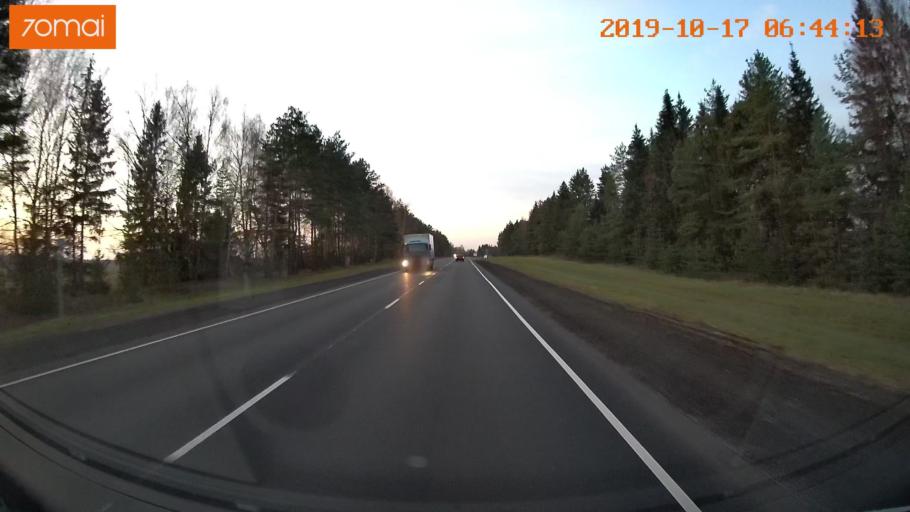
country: RU
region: Vladimir
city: Kideksha
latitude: 56.5758
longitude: 40.5546
